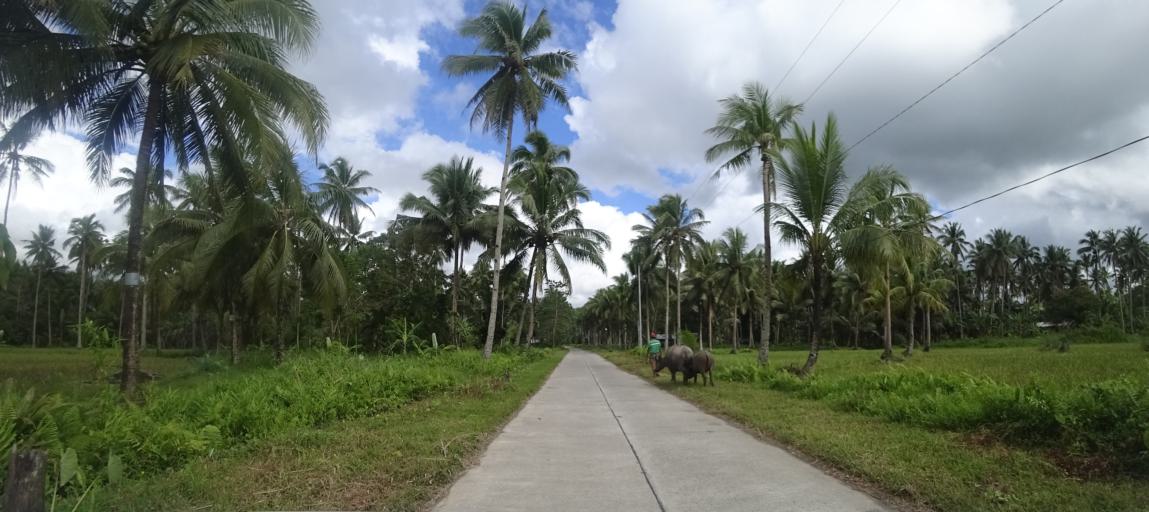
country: PH
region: Eastern Visayas
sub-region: Province of Leyte
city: Bugho
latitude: 10.8245
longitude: 124.9249
